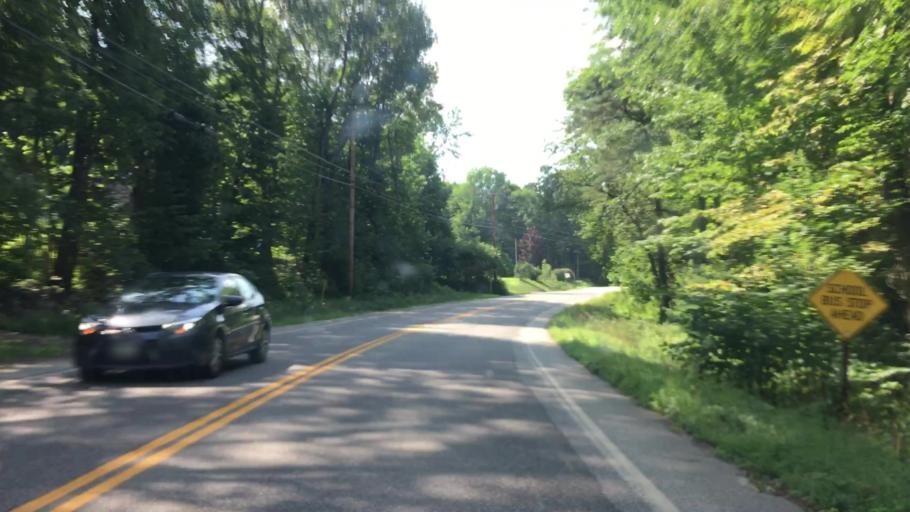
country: US
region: Maine
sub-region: Cumberland County
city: Raymond
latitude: 43.9228
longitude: -70.4353
